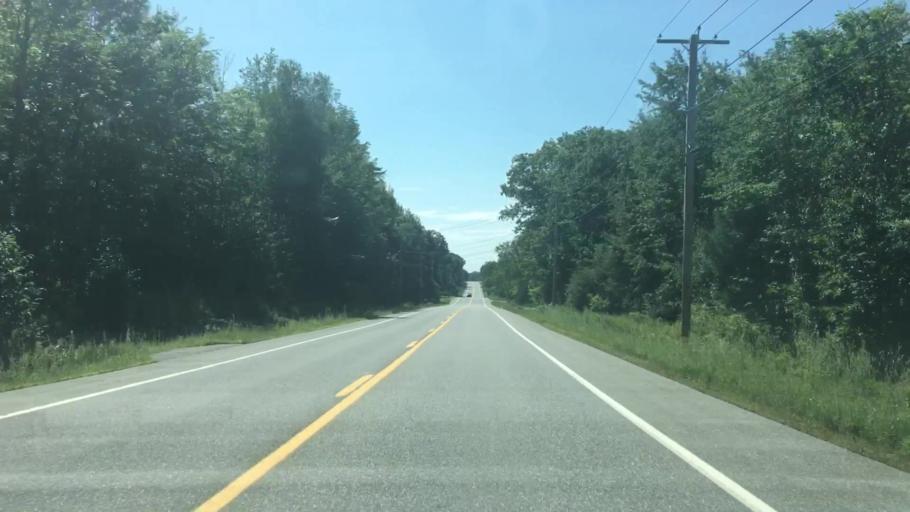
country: US
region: Maine
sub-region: Kennebec County
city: Monmouth
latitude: 44.1866
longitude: -69.9844
